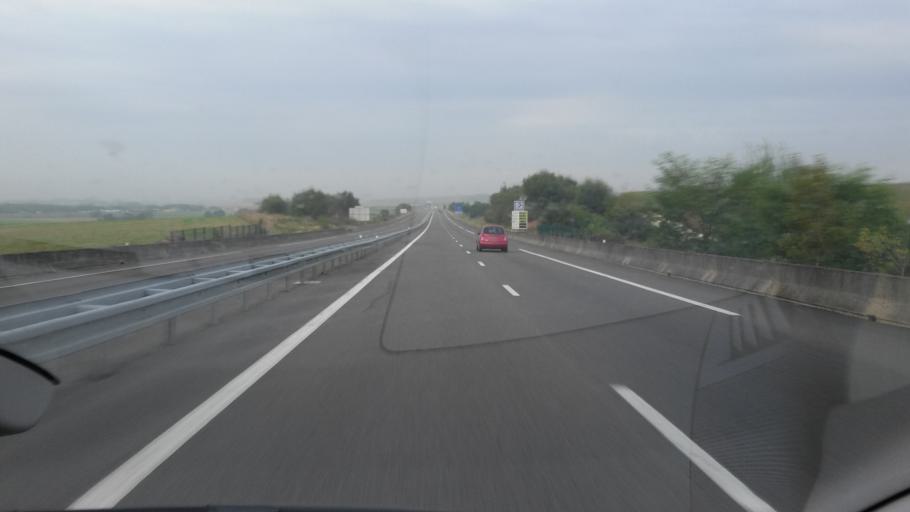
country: FR
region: Champagne-Ardenne
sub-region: Departement des Ardennes
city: Attigny
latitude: 49.6018
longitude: 4.5159
